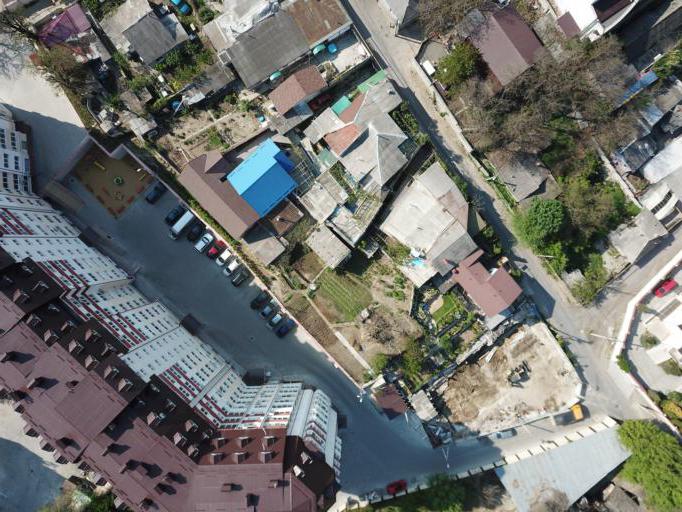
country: MD
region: Chisinau
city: Chisinau
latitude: 47.0104
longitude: 28.8526
